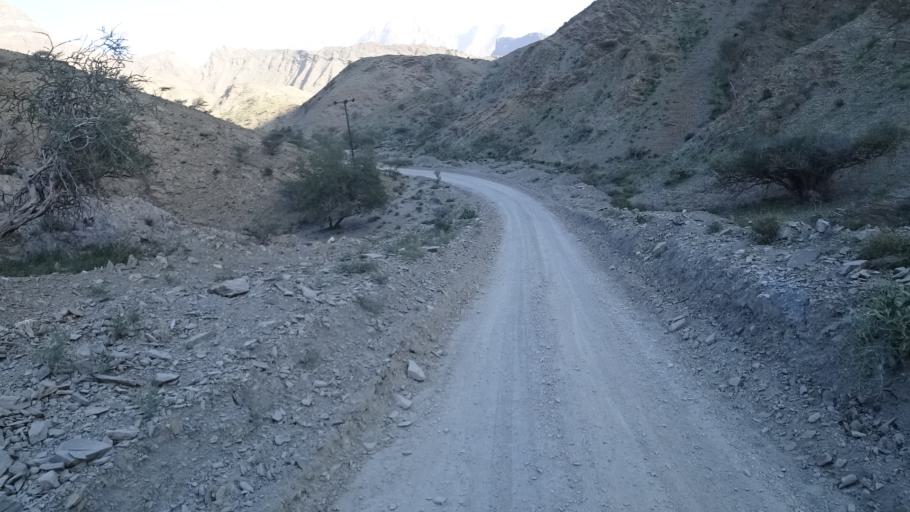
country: OM
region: Al Batinah
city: Rustaq
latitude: 23.2718
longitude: 57.3845
